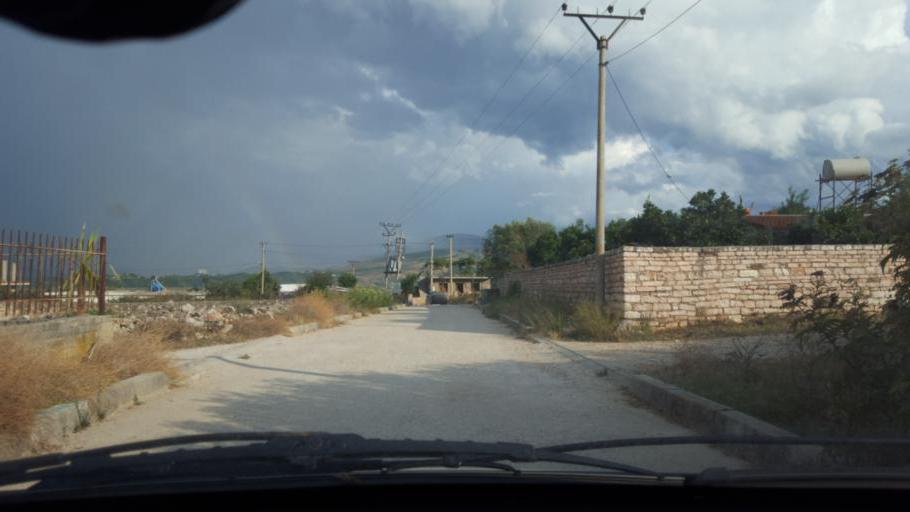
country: AL
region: Vlore
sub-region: Rrethi i Sarandes
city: Sarande
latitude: 39.8402
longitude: 20.0222
